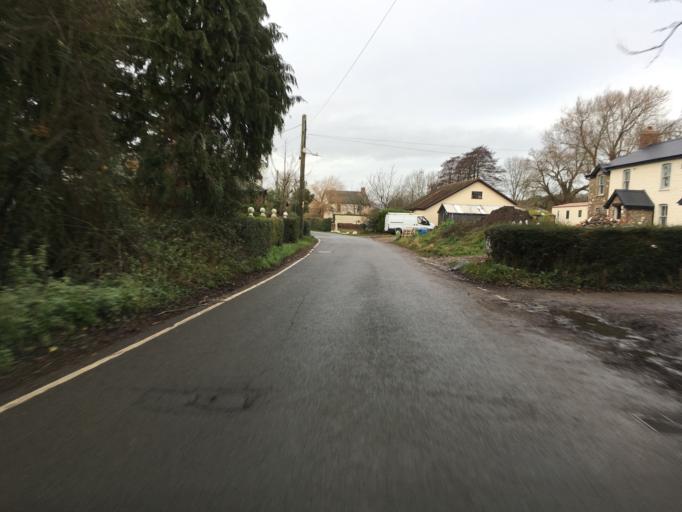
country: GB
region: Wales
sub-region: Monmouthshire
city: Magor
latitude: 51.5738
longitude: -2.8232
